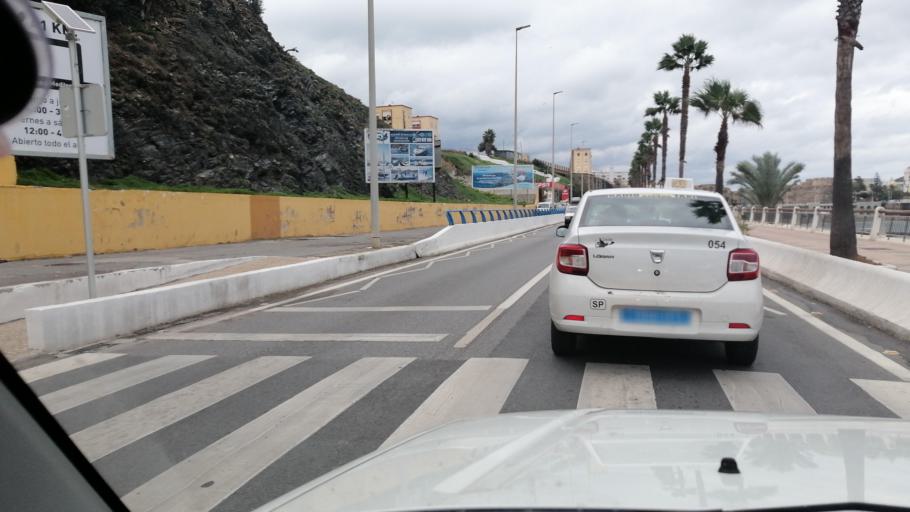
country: ES
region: Ceuta
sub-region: Ceuta
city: Ceuta
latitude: 35.8841
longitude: -5.3236
